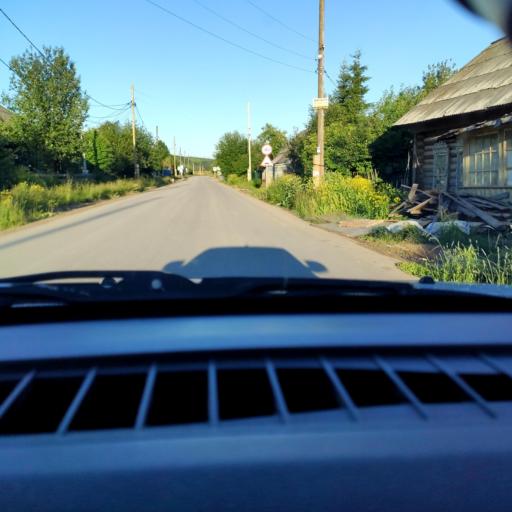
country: RU
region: Perm
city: Novyye Lyady
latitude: 58.1849
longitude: 56.5436
